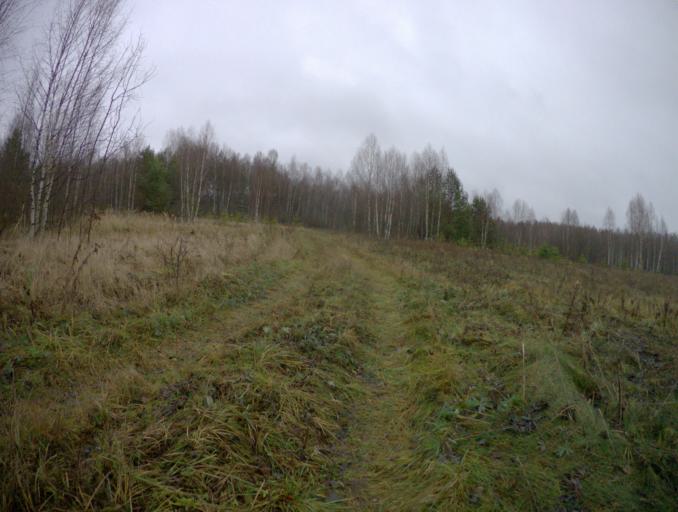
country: RU
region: Vladimir
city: Golovino
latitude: 55.9800
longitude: 40.4999
